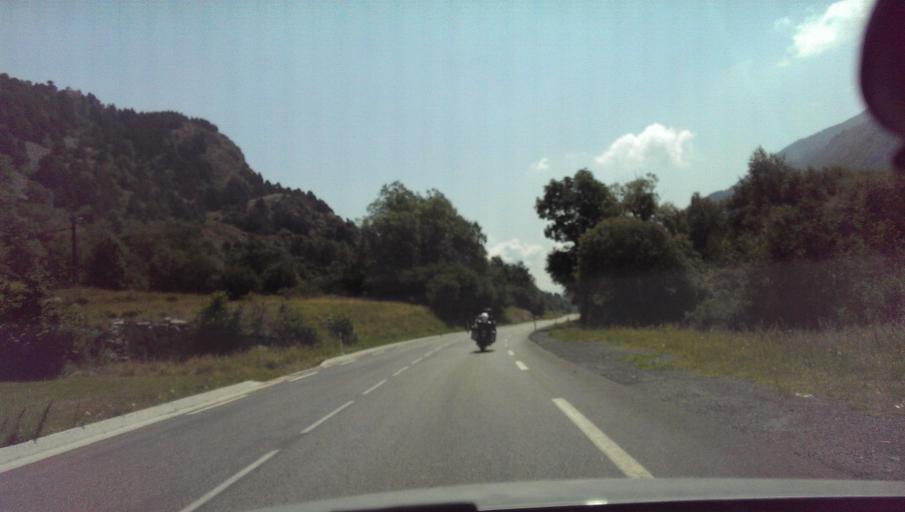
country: ES
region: Catalonia
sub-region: Provincia de Girona
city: Meranges
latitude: 42.5090
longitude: 1.8312
